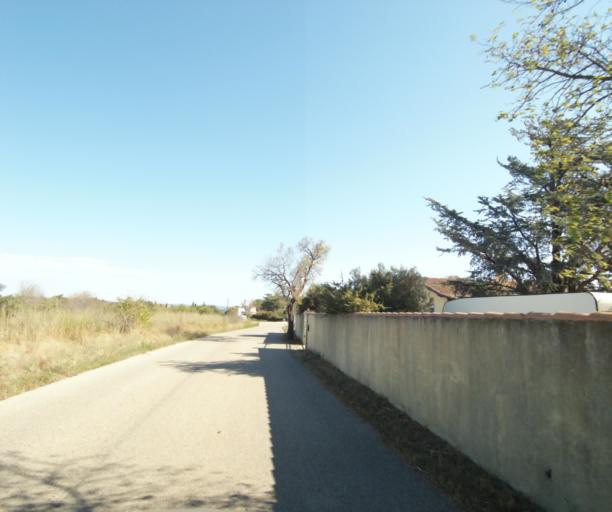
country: FR
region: Languedoc-Roussillon
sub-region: Departement du Gard
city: Bouillargues
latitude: 43.7944
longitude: 4.4183
